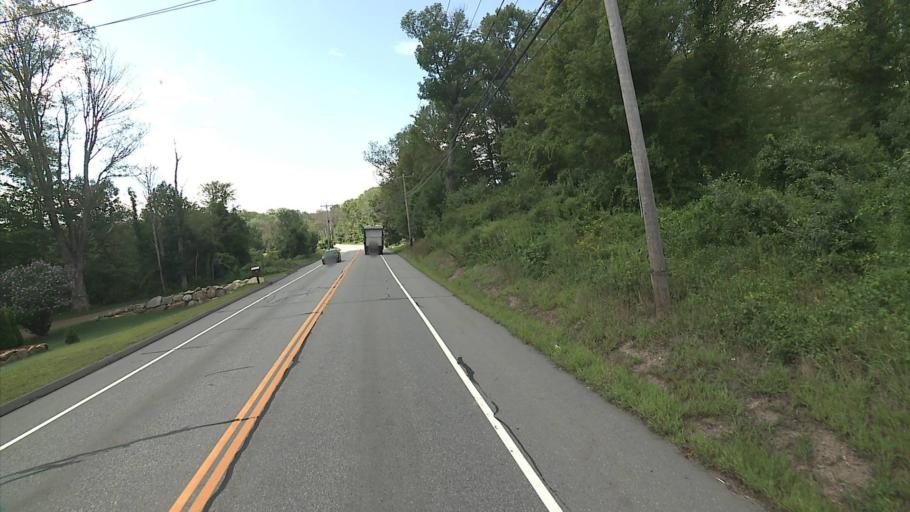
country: US
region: Connecticut
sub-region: Tolland County
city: Crystal Lake
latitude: 41.9740
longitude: -72.3701
